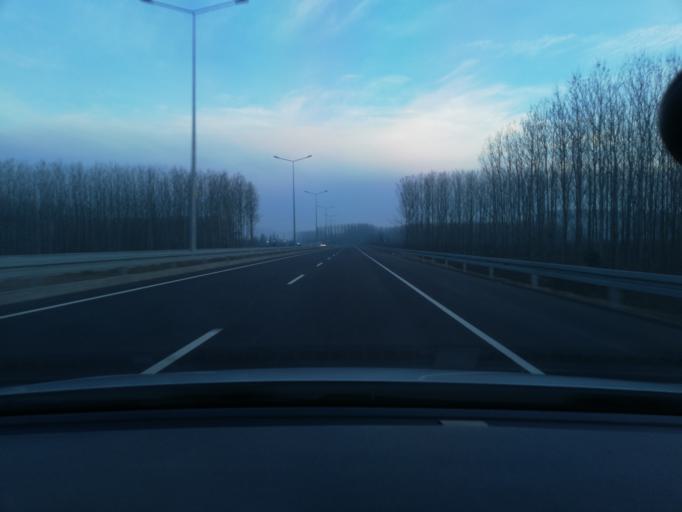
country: TR
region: Duzce
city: Duzce
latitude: 40.8077
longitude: 31.1688
